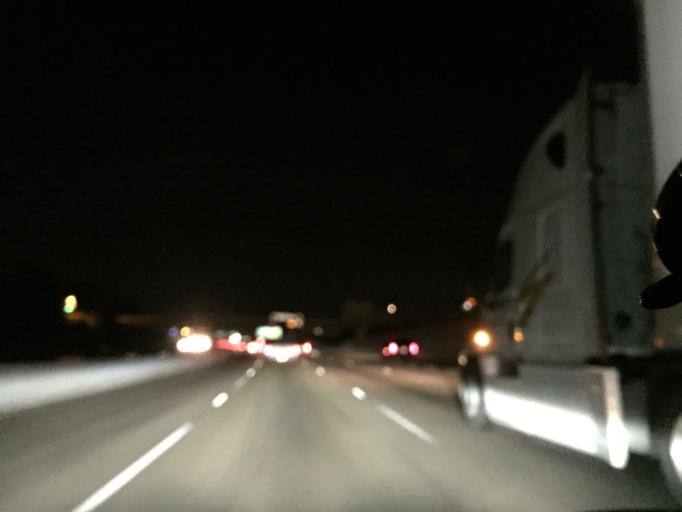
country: US
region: California
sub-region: Alameda County
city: San Leandro
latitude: 37.7142
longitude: -122.1720
